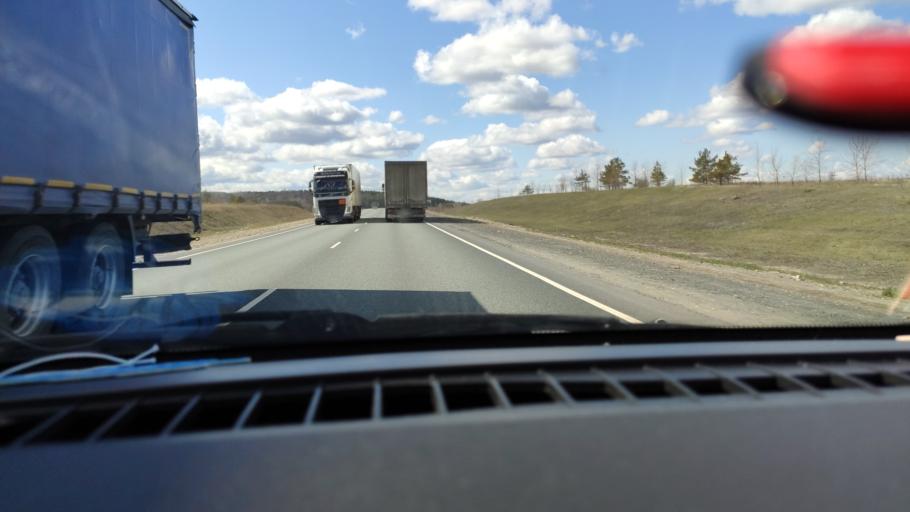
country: RU
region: Saratov
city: Khvalynsk
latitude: 52.5475
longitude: 48.0698
